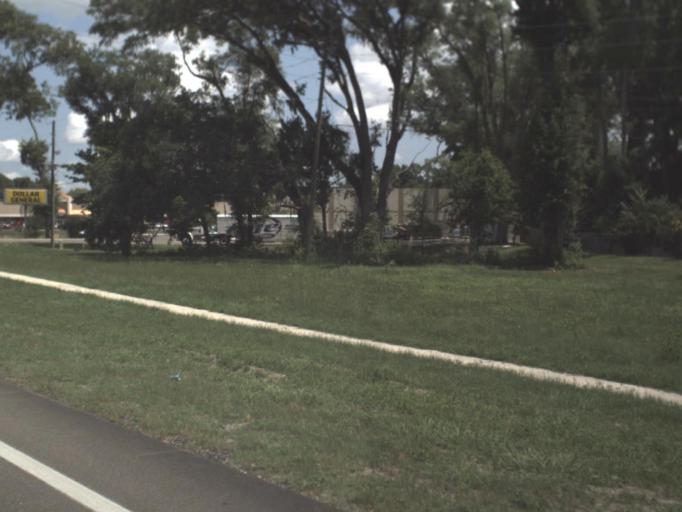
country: US
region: Florida
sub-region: Alachua County
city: High Springs
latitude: 29.8386
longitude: -82.6019
